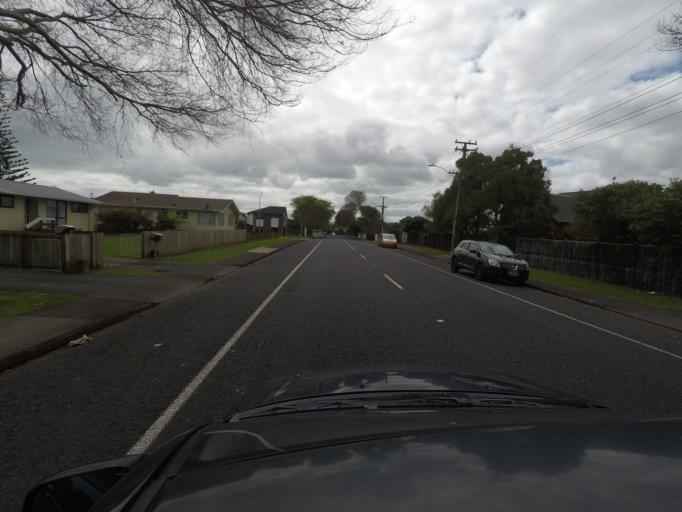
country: NZ
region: Auckland
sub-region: Auckland
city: Tamaki
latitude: -36.9371
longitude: 174.8583
